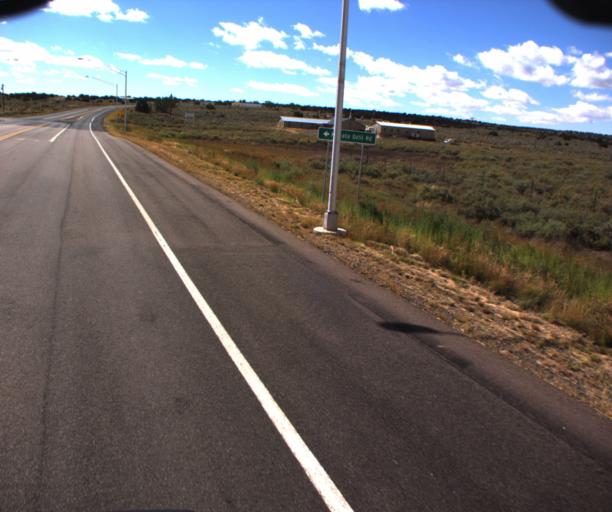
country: US
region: Arizona
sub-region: Apache County
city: Houck
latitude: 35.1988
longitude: -109.3327
